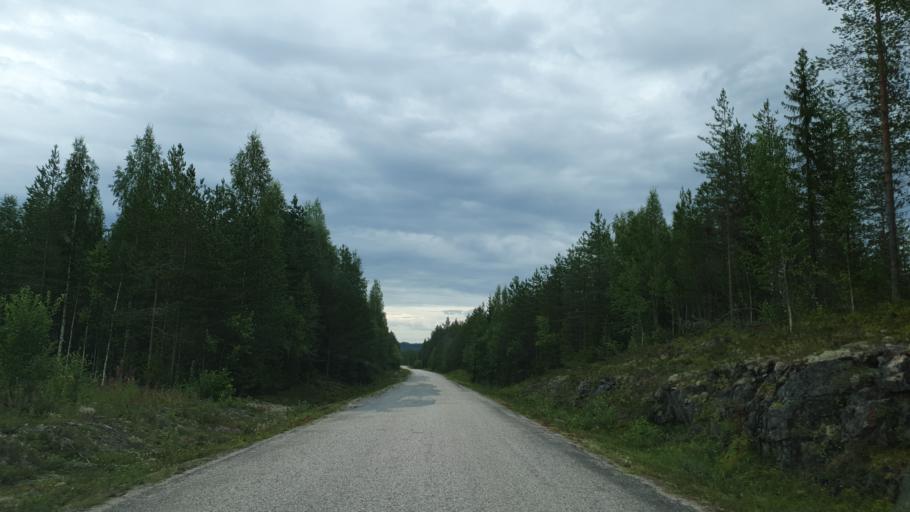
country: FI
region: Kainuu
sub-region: Kehys-Kainuu
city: Kuhmo
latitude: 64.3460
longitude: 29.2678
